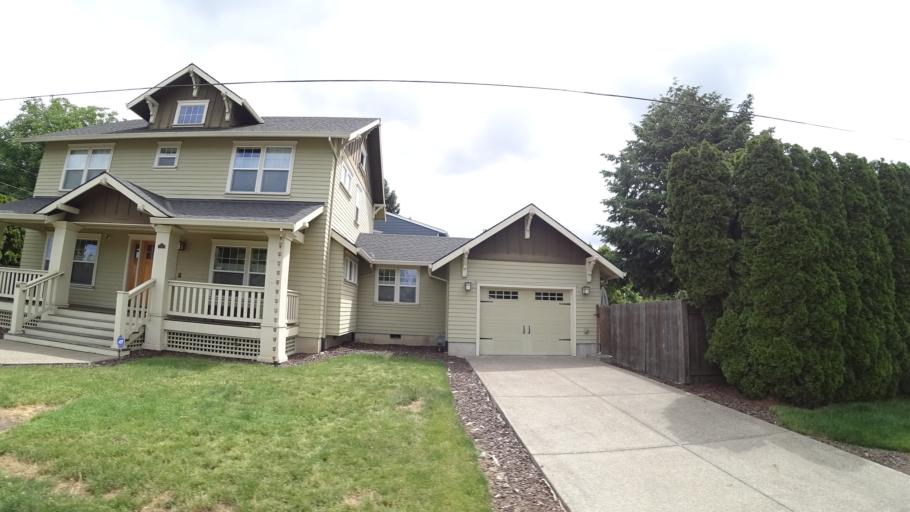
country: US
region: Oregon
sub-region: Multnomah County
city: Portland
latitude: 45.5679
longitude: -122.6092
